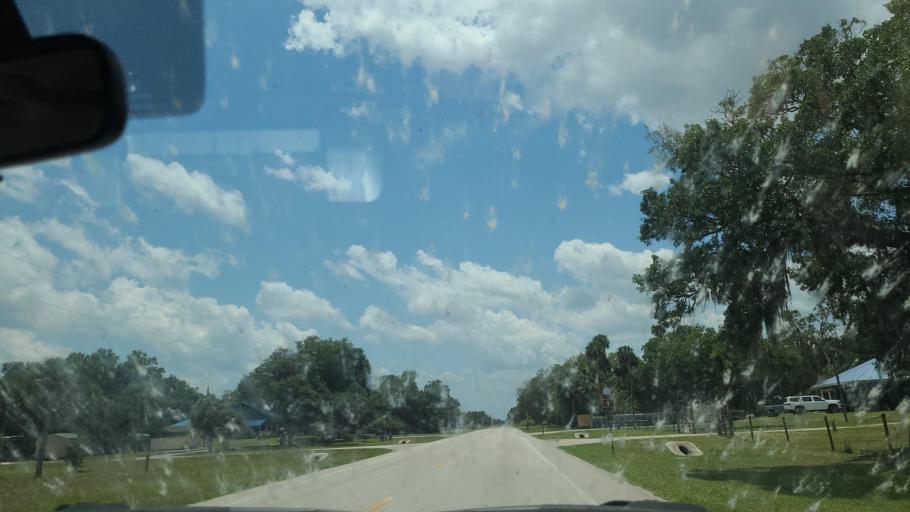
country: US
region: Florida
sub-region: Glades County
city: Buckhead Ridge
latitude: 27.0955
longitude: -81.0701
